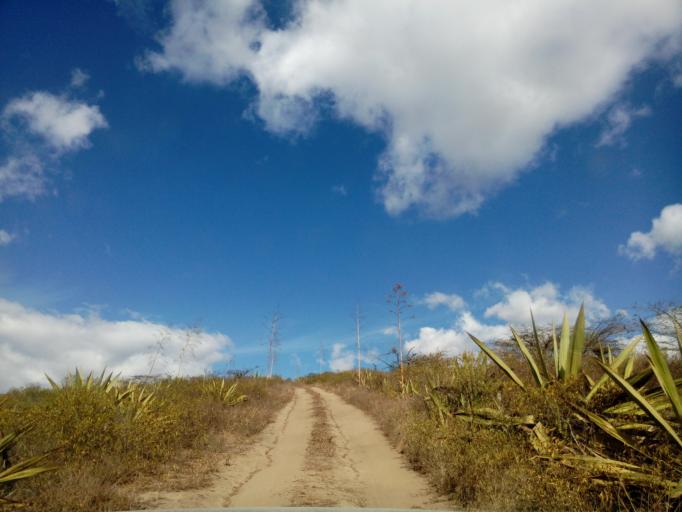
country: EC
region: Imbabura
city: Atuntaqui
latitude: 0.4180
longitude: -78.1868
